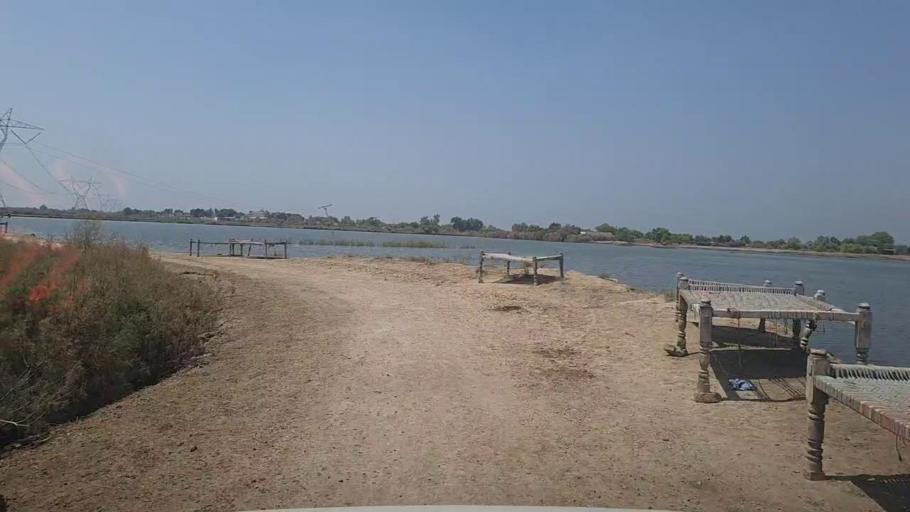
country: PK
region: Sindh
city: Kandhkot
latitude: 28.3196
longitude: 69.3734
